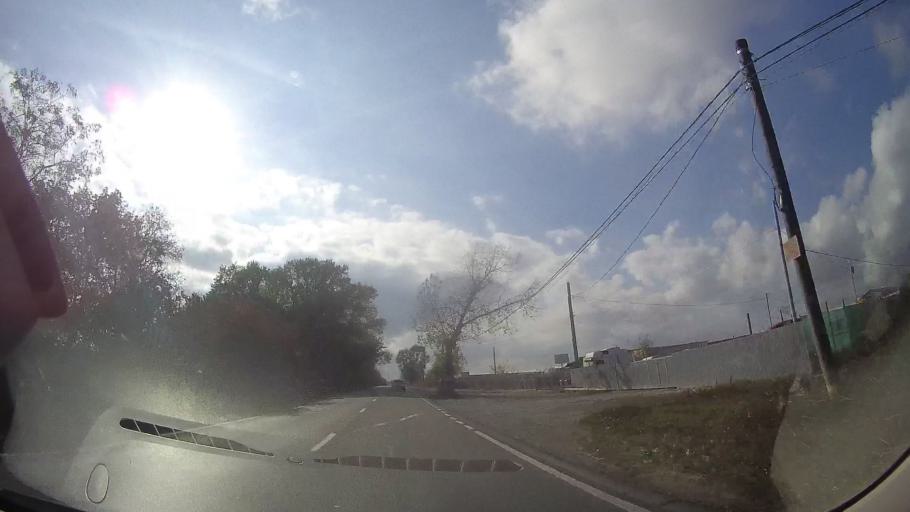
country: RO
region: Constanta
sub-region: Comuna Agigea
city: Agigea
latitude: 44.0848
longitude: 28.6070
